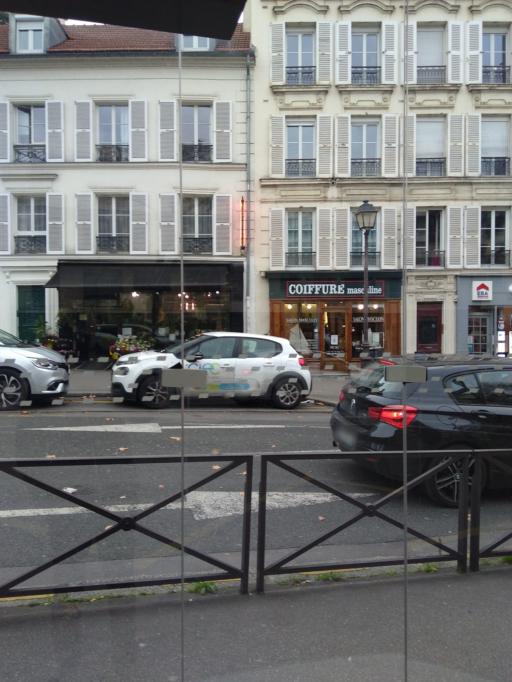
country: FR
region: Ile-de-France
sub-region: Departement du Val-de-Marne
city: Saint-Mande
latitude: 48.8445
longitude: 2.4064
